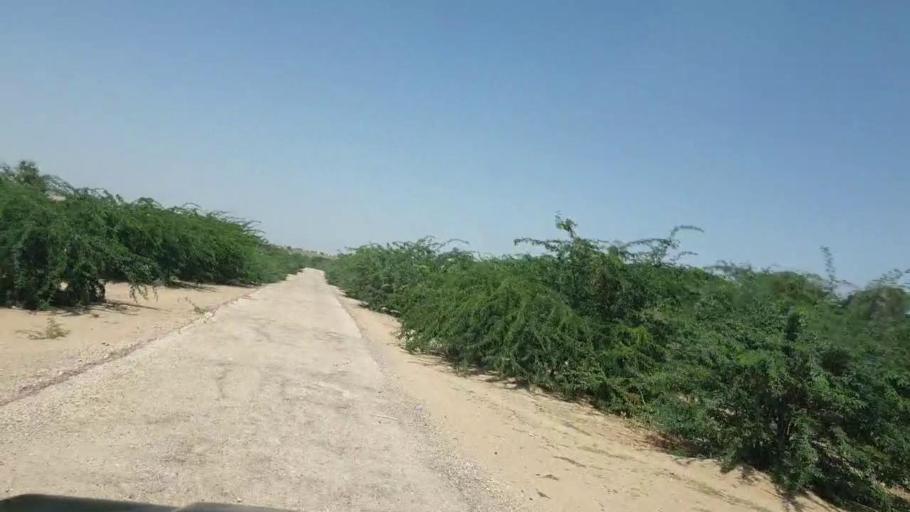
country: PK
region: Sindh
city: Chor
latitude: 25.4052
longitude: 70.3088
